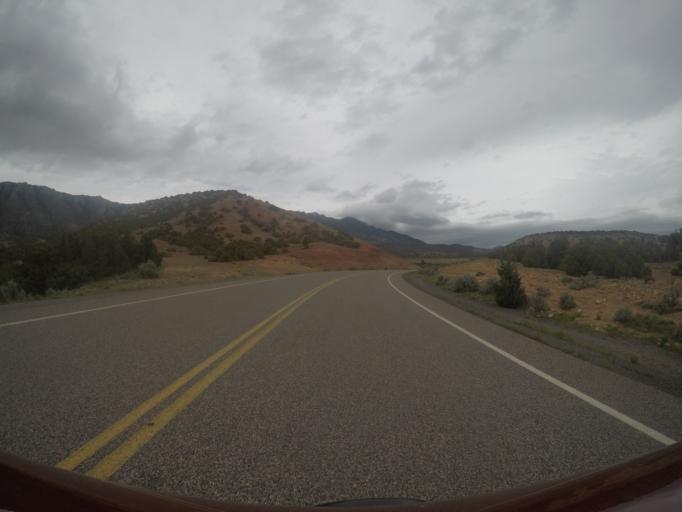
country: US
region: Wyoming
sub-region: Big Horn County
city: Lovell
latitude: 45.0746
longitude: -108.2577
